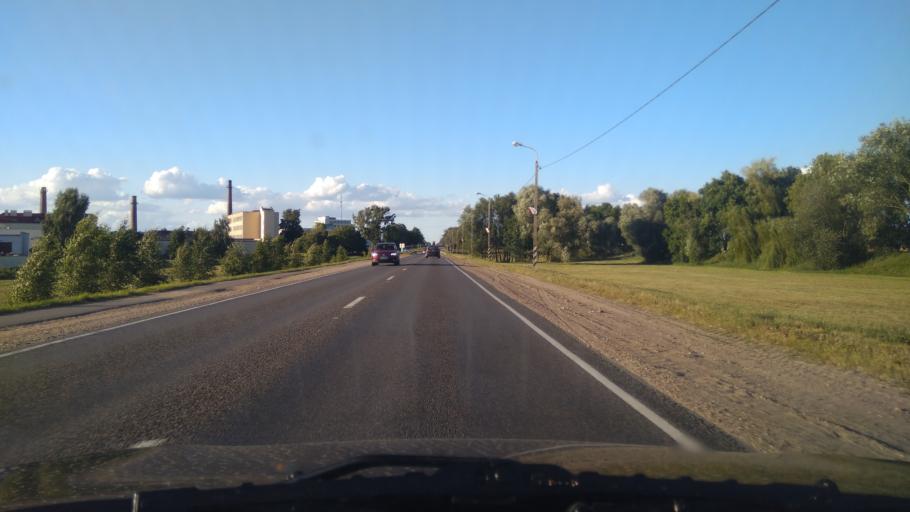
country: BY
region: Brest
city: Pruzhany
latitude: 52.5586
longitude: 24.4784
